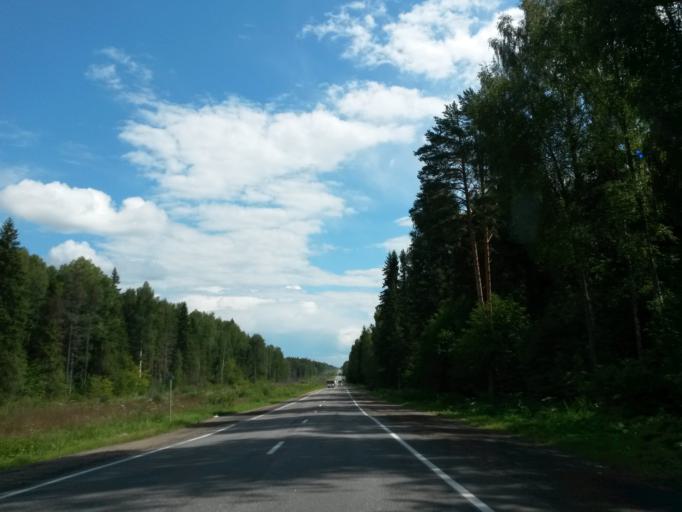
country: RU
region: Jaroslavl
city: Gavrilov-Yam
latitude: 57.2680
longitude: 39.9817
